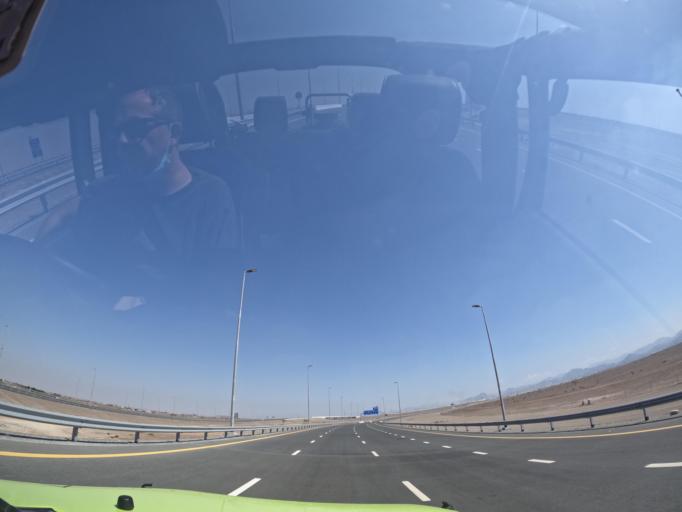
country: AE
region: Ash Shariqah
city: Adh Dhayd
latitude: 25.1137
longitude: 55.9368
